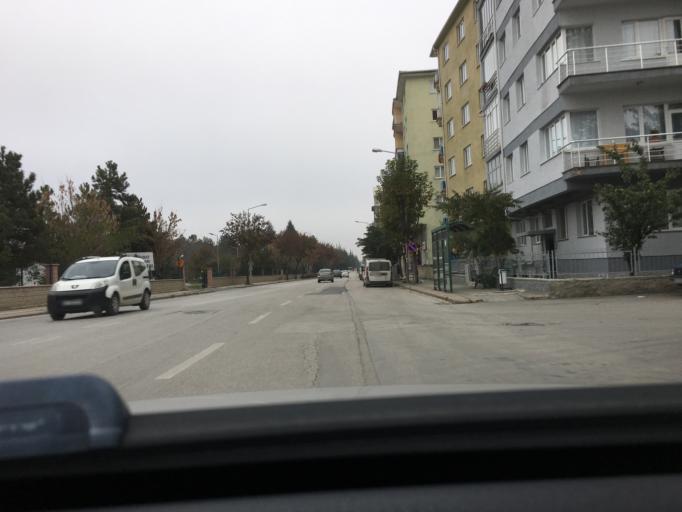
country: TR
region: Eskisehir
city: Eskisehir
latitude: 39.7715
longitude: 30.4861
